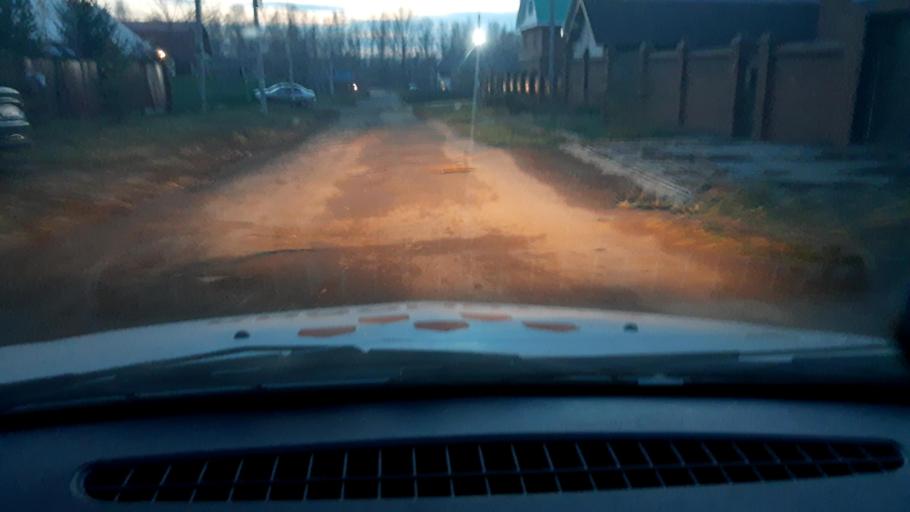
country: RU
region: Bashkortostan
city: Iglino
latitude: 54.7782
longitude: 56.2347
